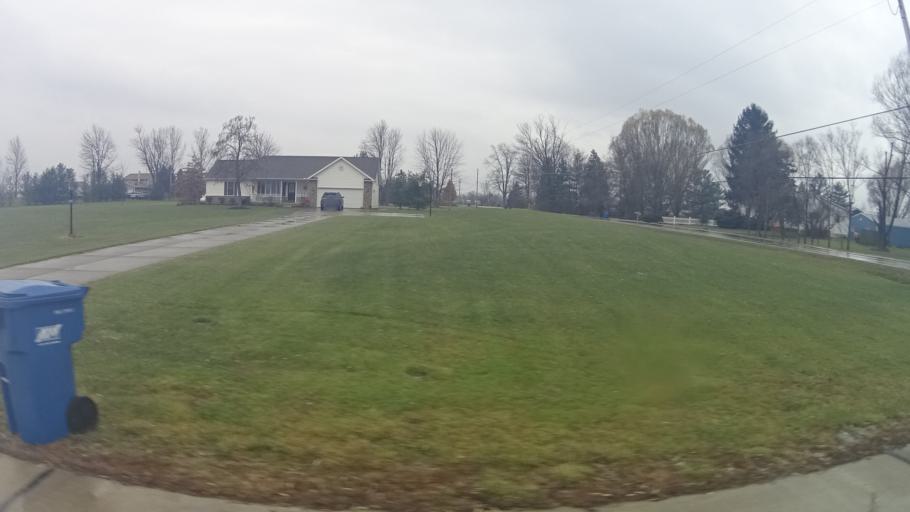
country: US
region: Ohio
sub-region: Lorain County
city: Lagrange
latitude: 41.2609
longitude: -82.1387
